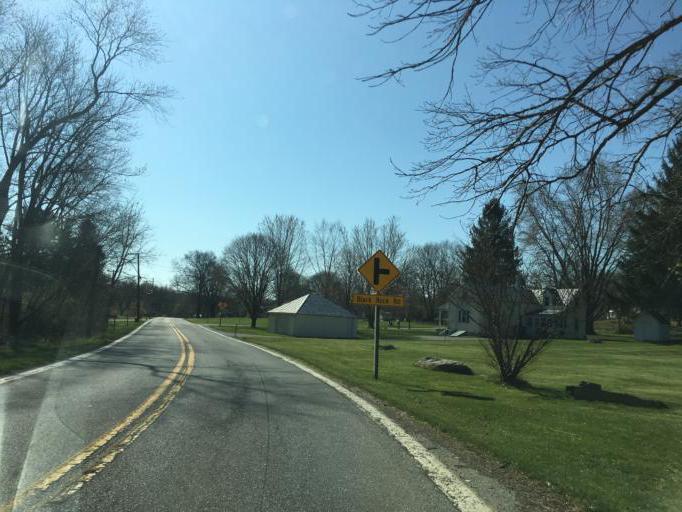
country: US
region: Maryland
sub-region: Washington County
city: Cavetown
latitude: 39.5785
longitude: -77.5561
